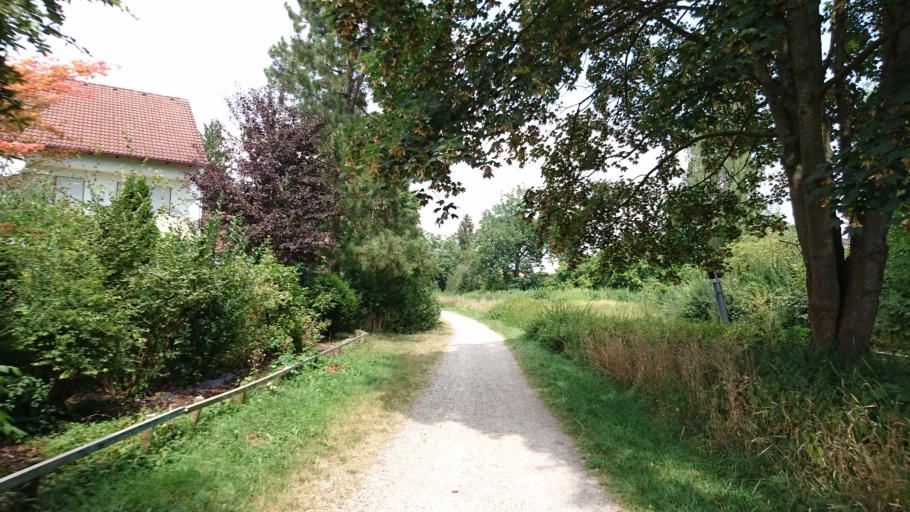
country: DE
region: Bavaria
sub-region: Swabia
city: Augsburg
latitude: 48.3878
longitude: 10.9285
